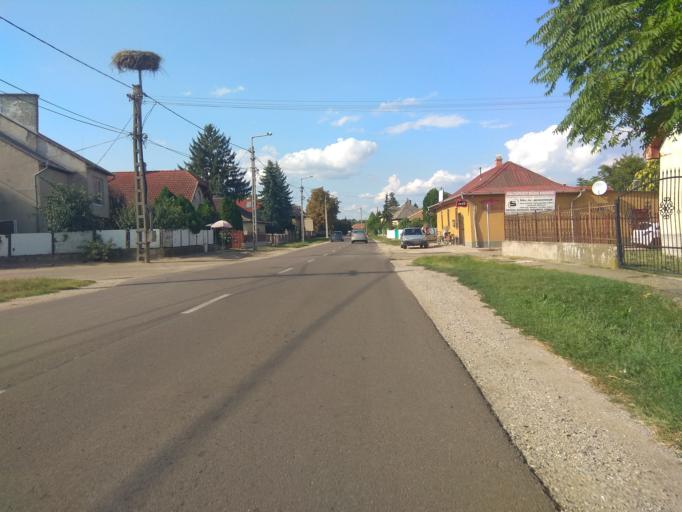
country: HU
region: Borsod-Abauj-Zemplen
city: Mezocsat
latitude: 47.8264
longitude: 20.9022
